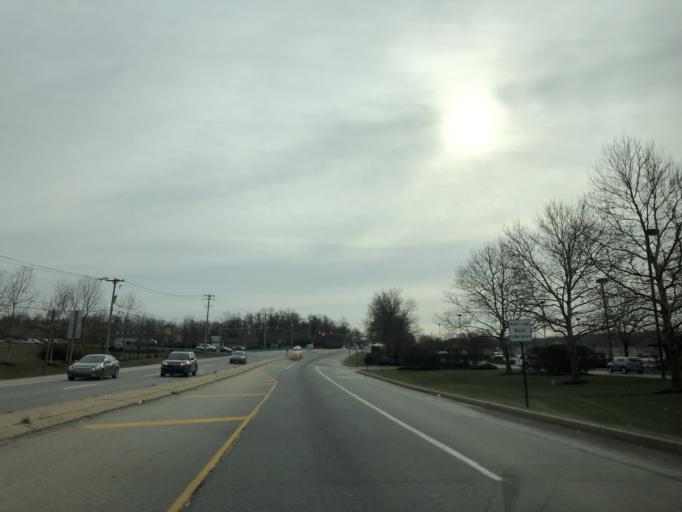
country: US
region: Pennsylvania
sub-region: Chester County
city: Downingtown
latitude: 40.0182
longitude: -75.6753
